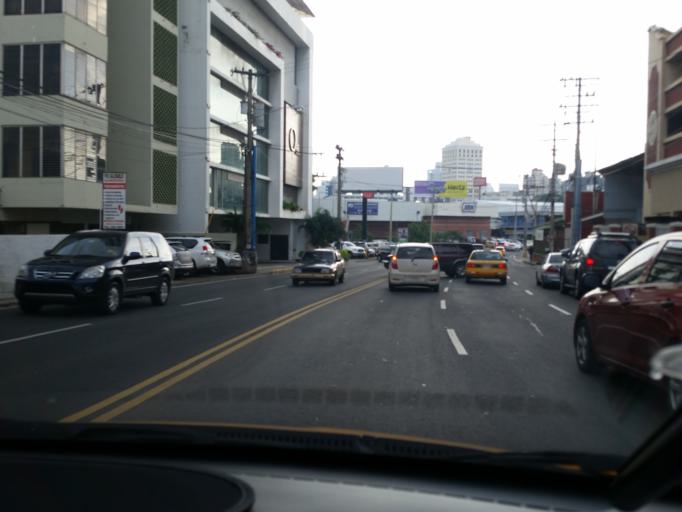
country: PA
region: Panama
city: Panama
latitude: 8.9931
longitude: -79.5169
